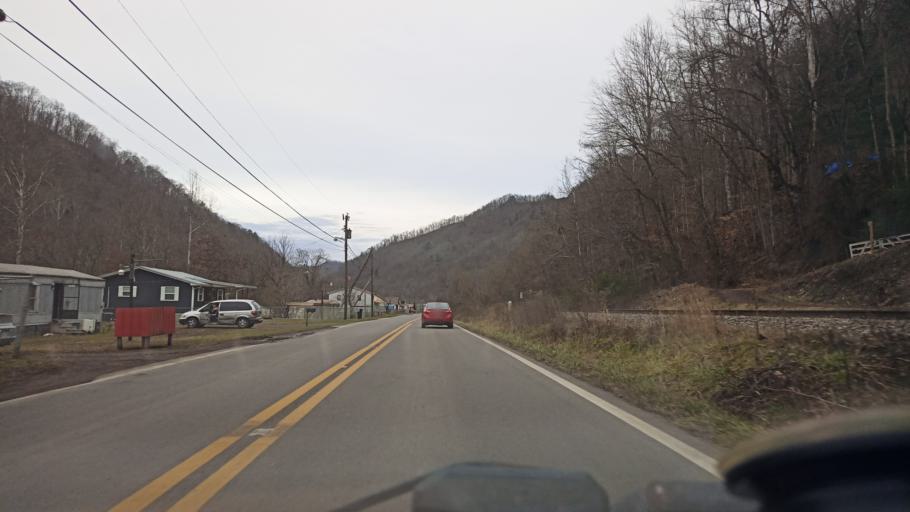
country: US
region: West Virginia
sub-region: Logan County
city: Mallory
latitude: 37.7089
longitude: -81.8670
